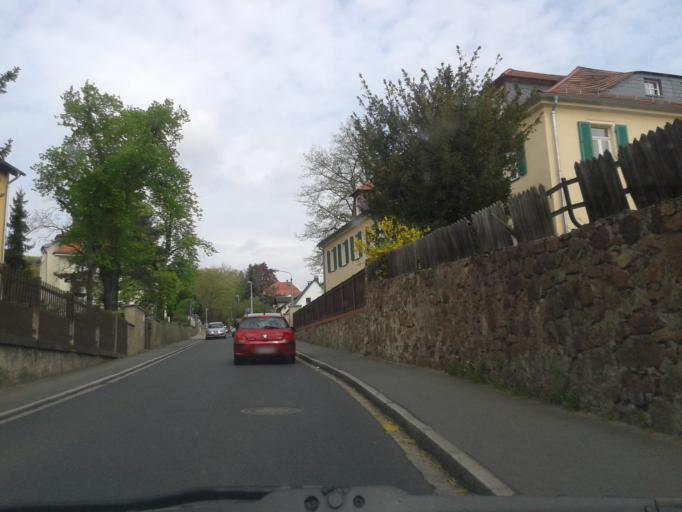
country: DE
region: Saxony
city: Radebeul
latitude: 51.1146
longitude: 13.6319
